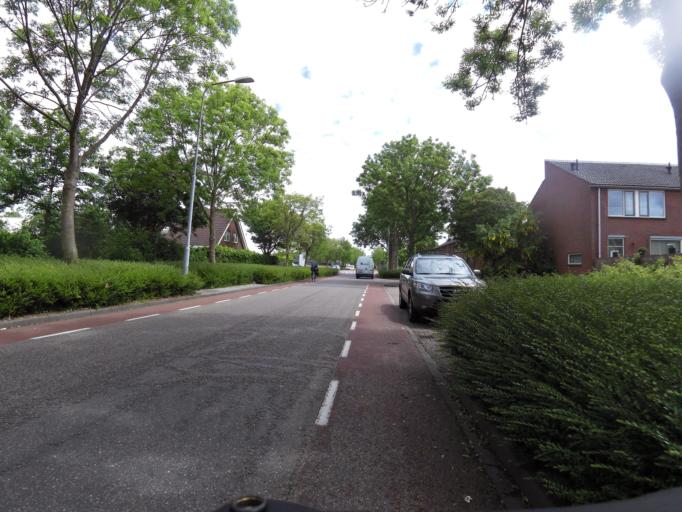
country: NL
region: Zeeland
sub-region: Schouwen-Duiveland
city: Scharendijke
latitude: 51.6526
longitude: 3.9051
